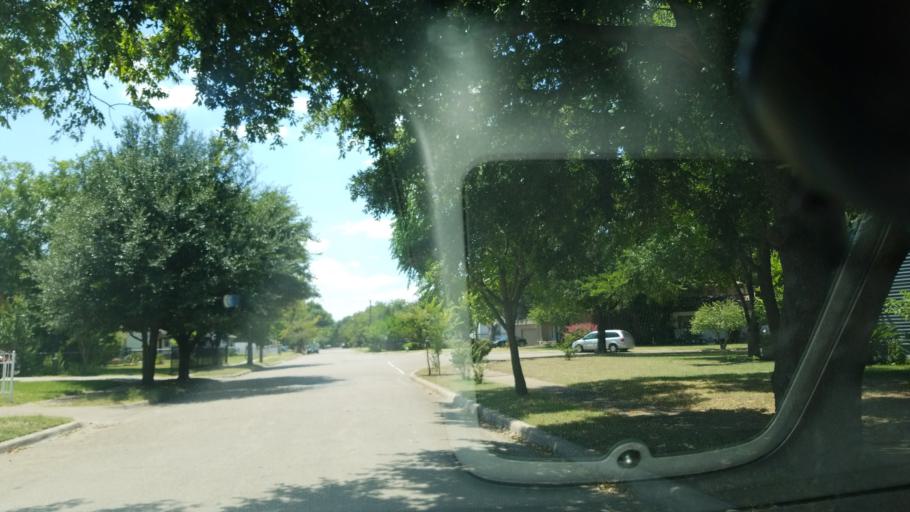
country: US
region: Texas
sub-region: Dallas County
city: Cockrell Hill
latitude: 32.7152
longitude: -96.8523
